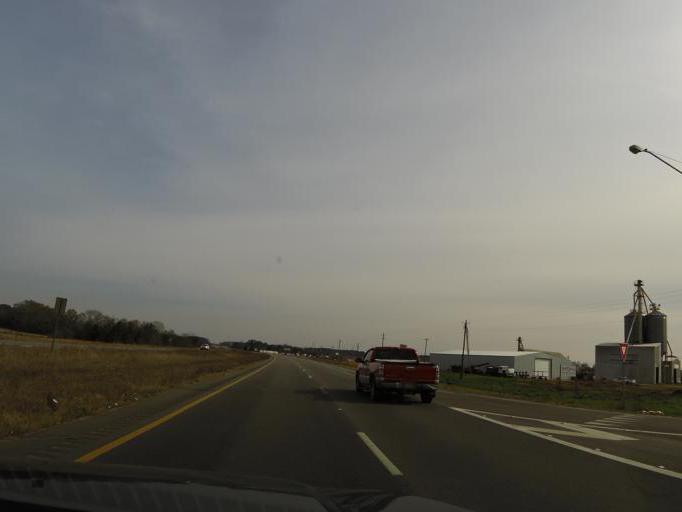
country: US
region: Alabama
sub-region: Houston County
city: Ashford
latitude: 31.1741
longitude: -85.2344
